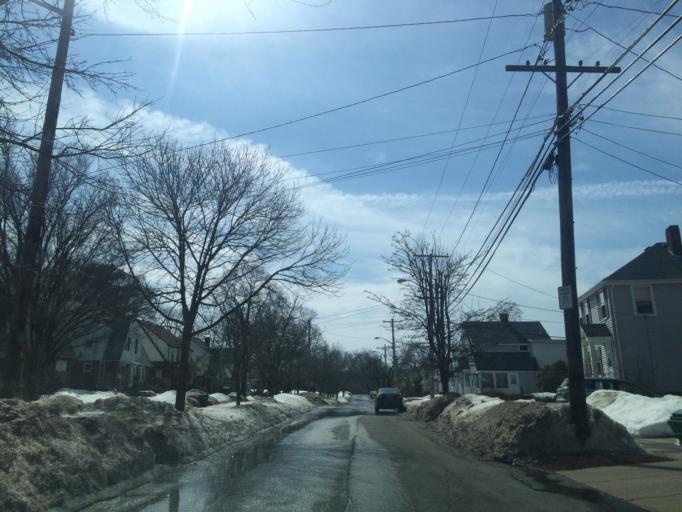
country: US
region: Massachusetts
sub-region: Middlesex County
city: Medford
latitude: 42.4299
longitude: -71.1102
